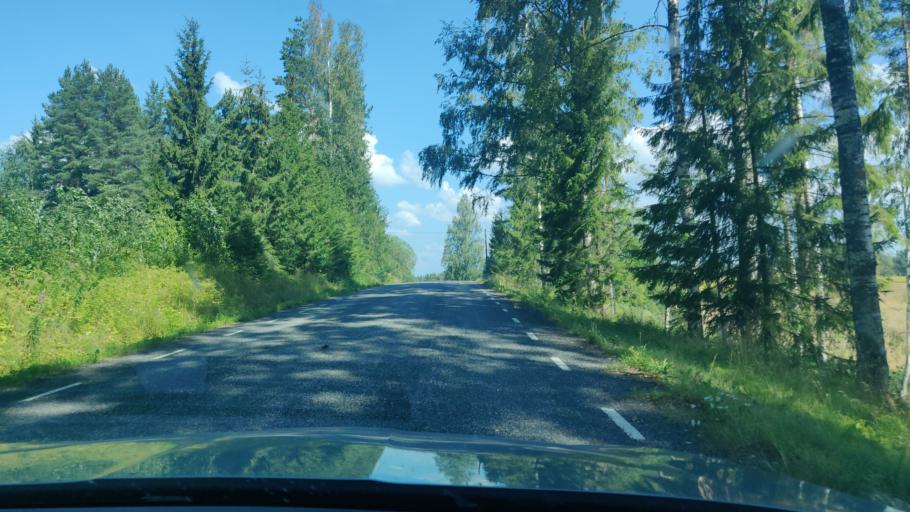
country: EE
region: Tartu
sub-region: Elva linn
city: Elva
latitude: 58.1390
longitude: 26.4774
